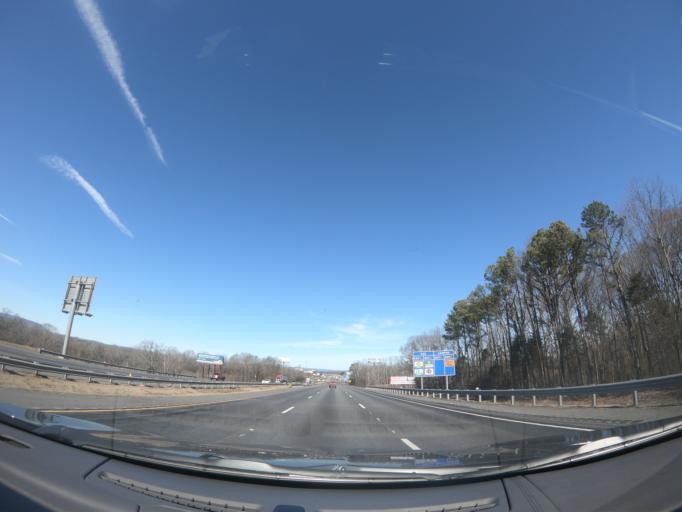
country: US
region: Georgia
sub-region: Catoosa County
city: Indian Springs
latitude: 34.9767
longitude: -85.1972
